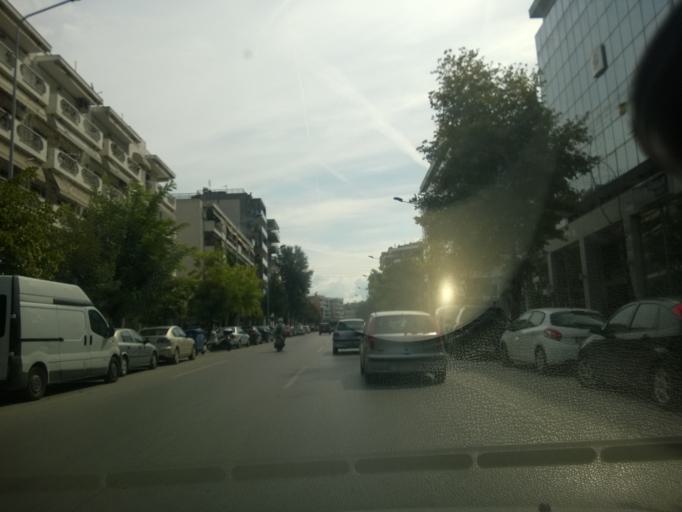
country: GR
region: Central Macedonia
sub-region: Nomos Thessalonikis
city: Kalamaria
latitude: 40.5860
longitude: 22.9562
